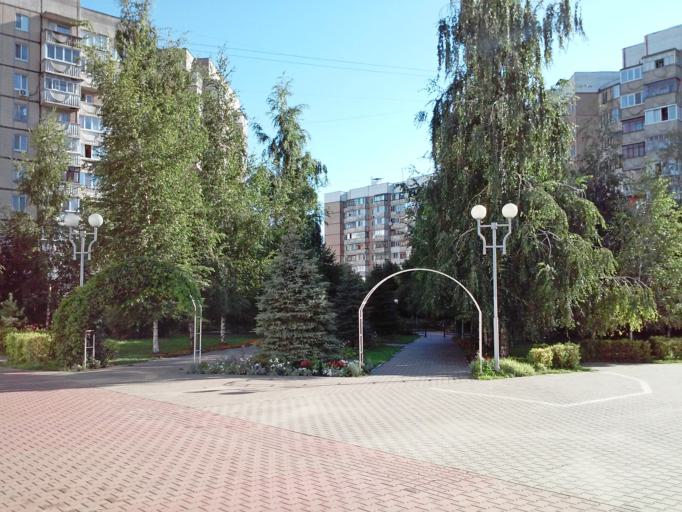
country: RU
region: Belgorod
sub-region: Belgorodskiy Rayon
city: Belgorod
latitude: 50.5584
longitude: 36.5685
